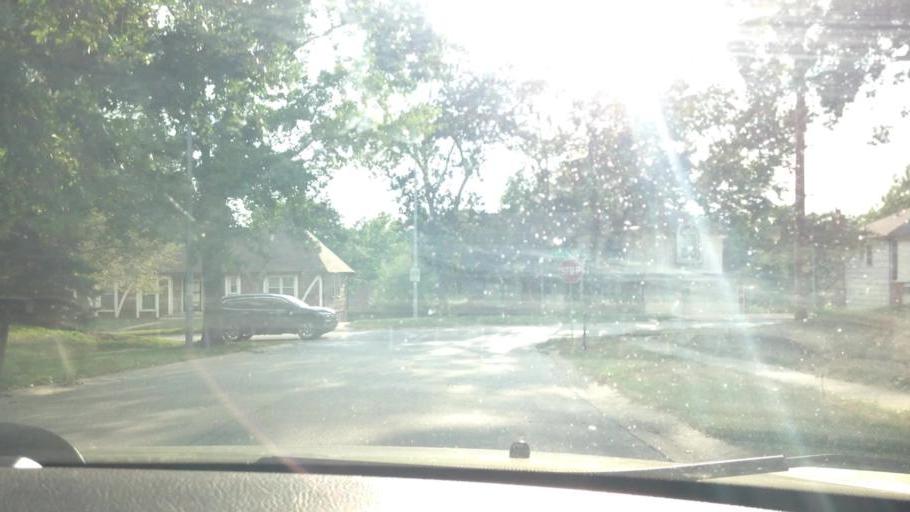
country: US
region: Missouri
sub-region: Platte County
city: Riverside
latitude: 39.2158
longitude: -94.6401
